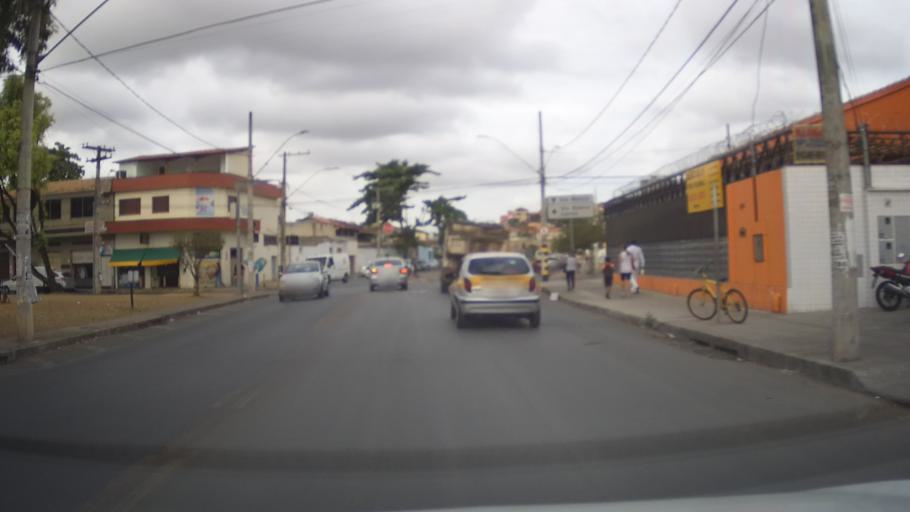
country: BR
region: Minas Gerais
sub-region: Belo Horizonte
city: Belo Horizonte
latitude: -19.8296
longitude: -43.9714
